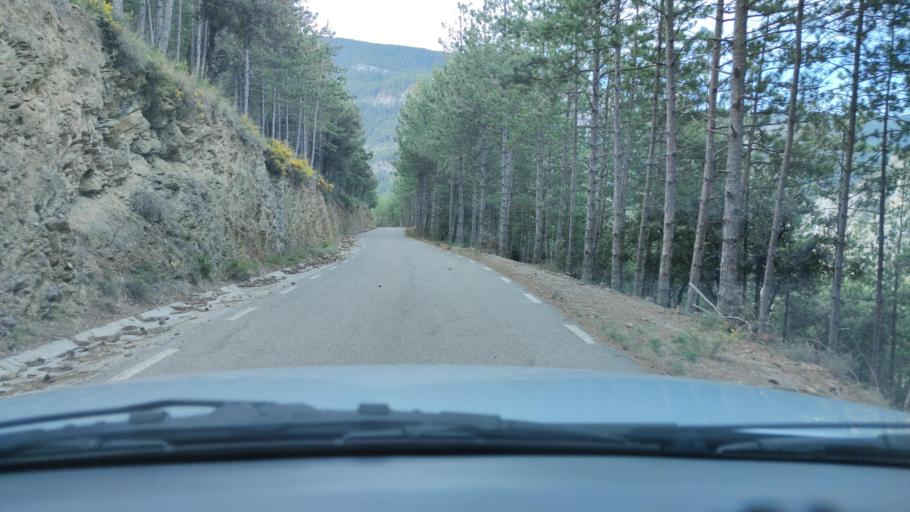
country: ES
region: Catalonia
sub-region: Provincia de Lleida
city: la Seu d'Urgell
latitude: 42.2437
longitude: 1.4252
